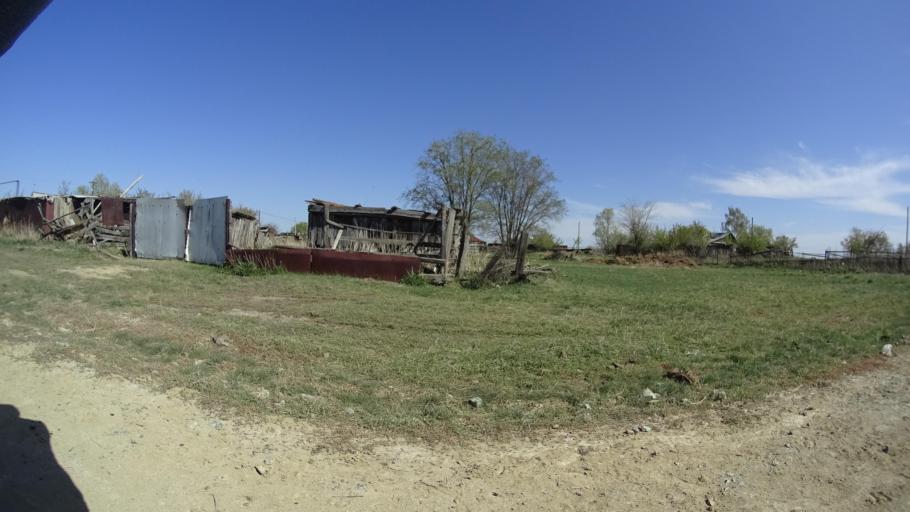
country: RU
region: Chelyabinsk
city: Chesma
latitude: 53.7990
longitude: 61.0175
